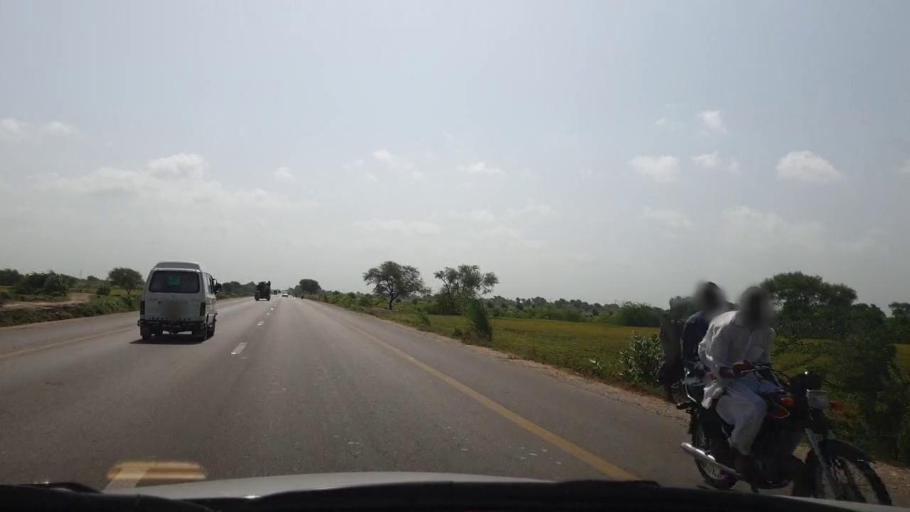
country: PK
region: Sindh
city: Matli
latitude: 24.9822
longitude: 68.6647
